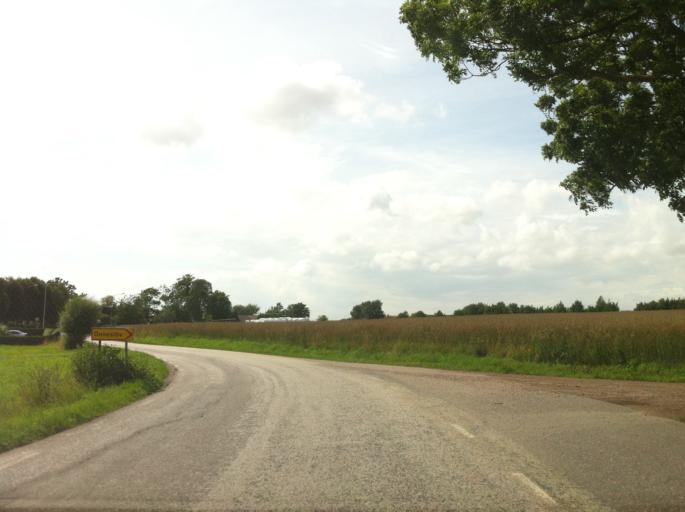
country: SE
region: Skane
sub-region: Lunds Kommun
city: Genarp
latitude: 55.5113
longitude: 13.4059
